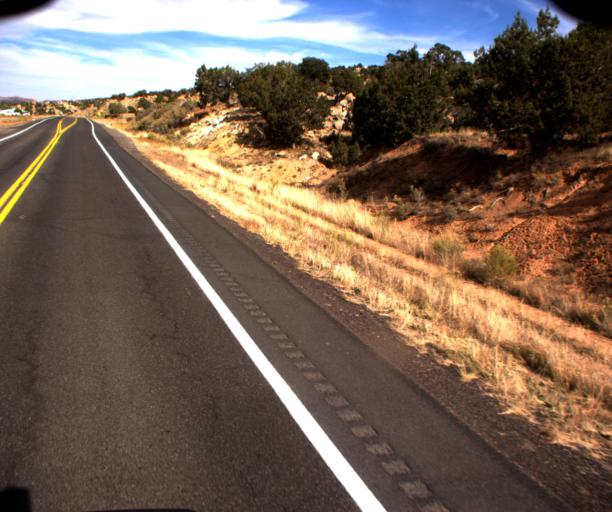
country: US
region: Arizona
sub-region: Navajo County
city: Kayenta
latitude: 36.6487
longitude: -110.4305
